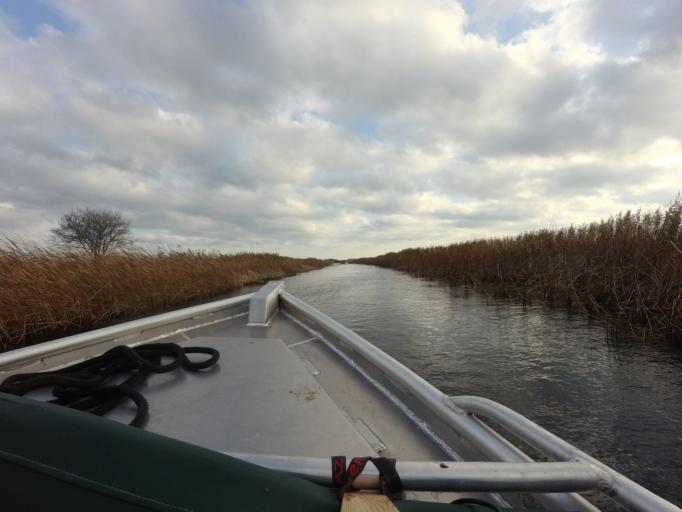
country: NL
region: Overijssel
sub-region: Gemeente Steenwijkerland
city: Blokzijl
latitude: 52.7512
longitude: 5.9635
